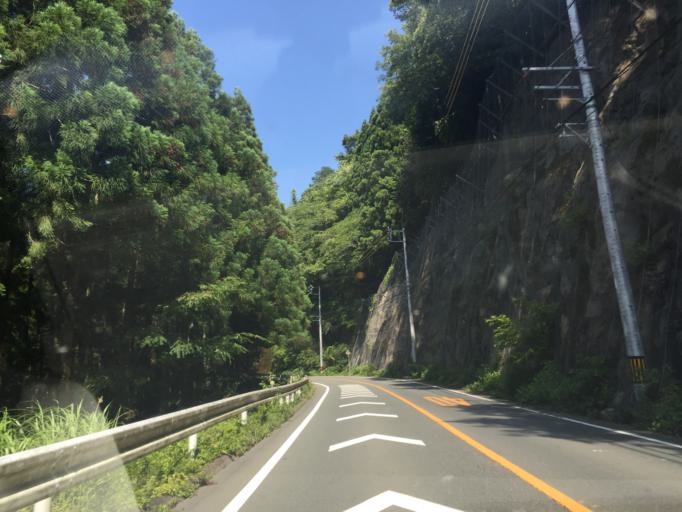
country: JP
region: Aichi
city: Shinshiro
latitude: 35.0182
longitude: 137.6918
